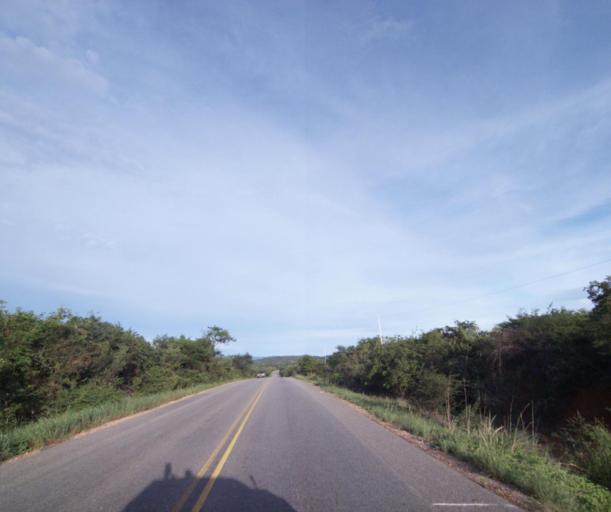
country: BR
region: Bahia
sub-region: Caetite
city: Caetite
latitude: -14.1675
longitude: -42.2450
